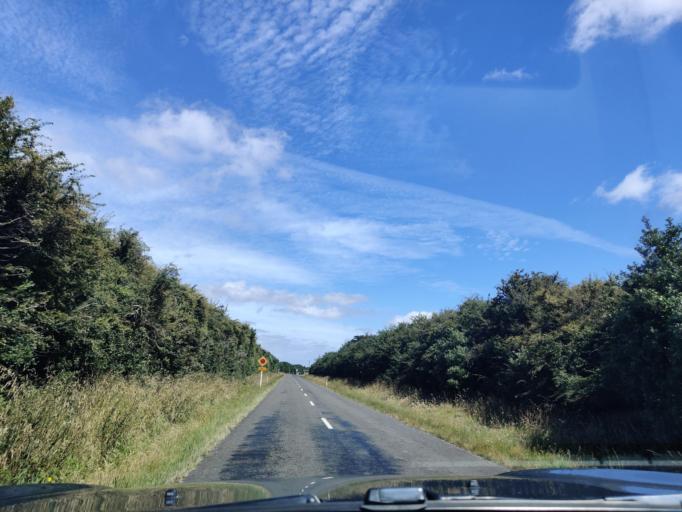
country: NZ
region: Manawatu-Wanganui
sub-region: Rangitikei District
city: Bulls
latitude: -40.1810
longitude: 175.4350
